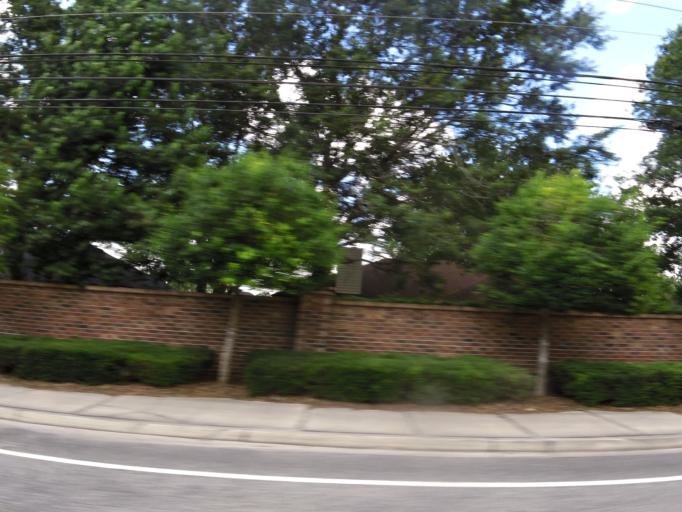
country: US
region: Florida
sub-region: Saint Johns County
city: Fruit Cove
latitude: 30.1407
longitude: -81.5260
